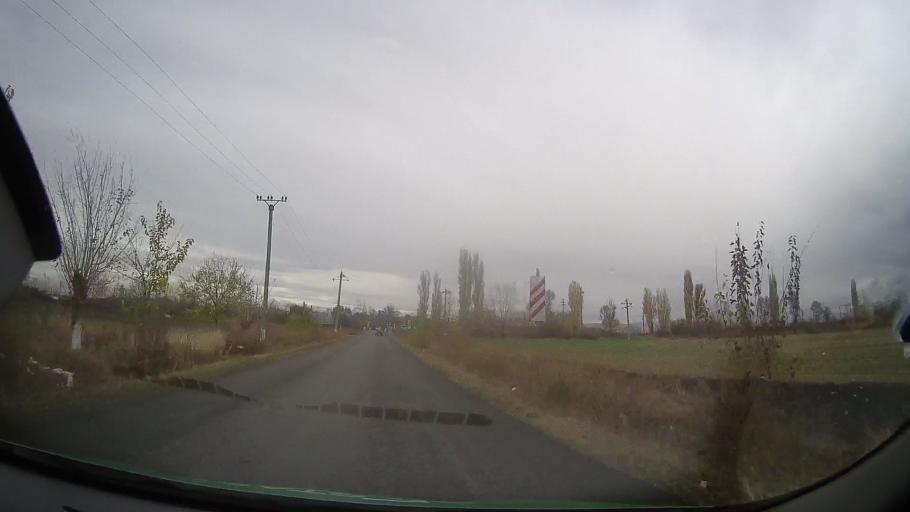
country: RO
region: Prahova
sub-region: Comuna Colceag
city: Inotesti
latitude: 44.9685
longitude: 26.3446
